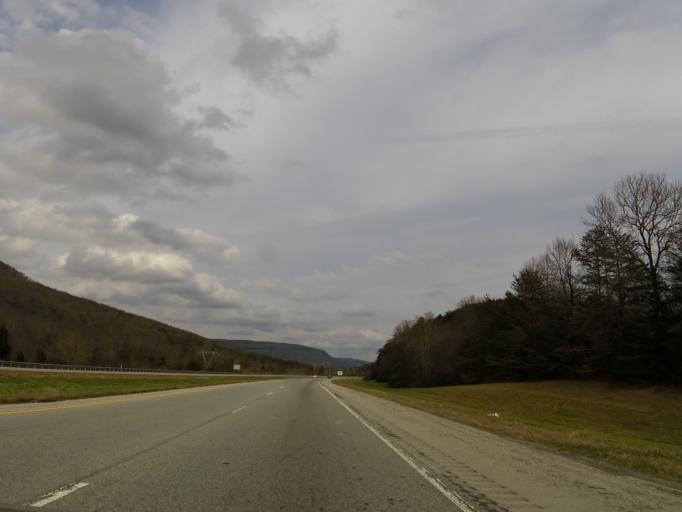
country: US
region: Tennessee
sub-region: Hamilton County
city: Walden
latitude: 35.1721
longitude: -85.2786
